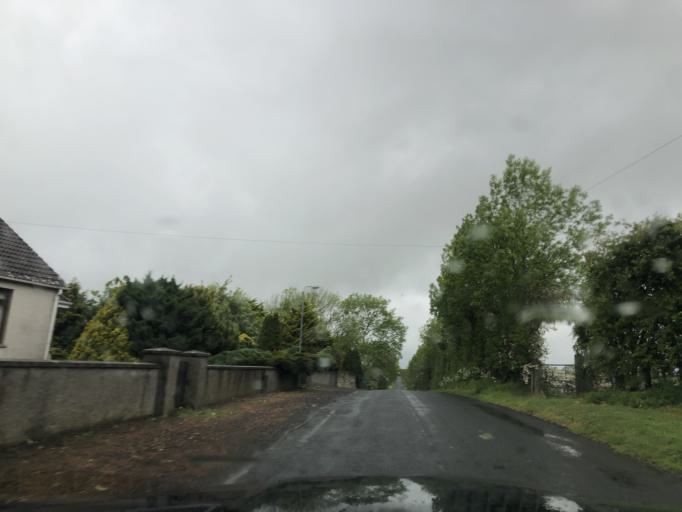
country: GB
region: Northern Ireland
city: Dunloy
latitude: 55.1168
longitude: -6.3524
